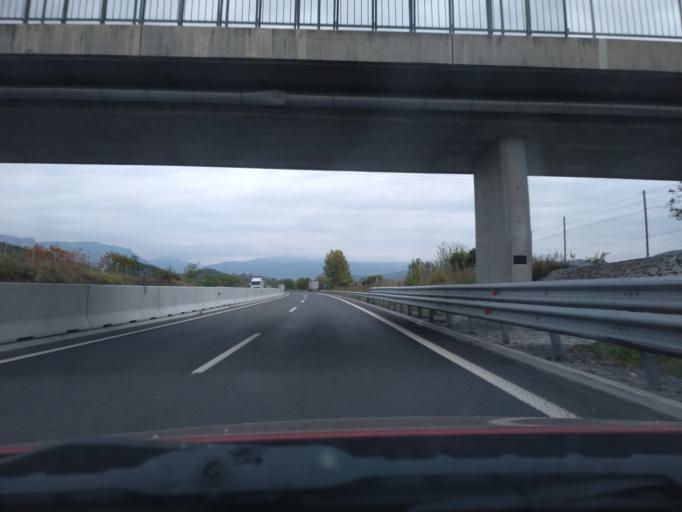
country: SI
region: Ajdovscina
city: Lokavec
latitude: 45.8874
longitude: 13.8205
